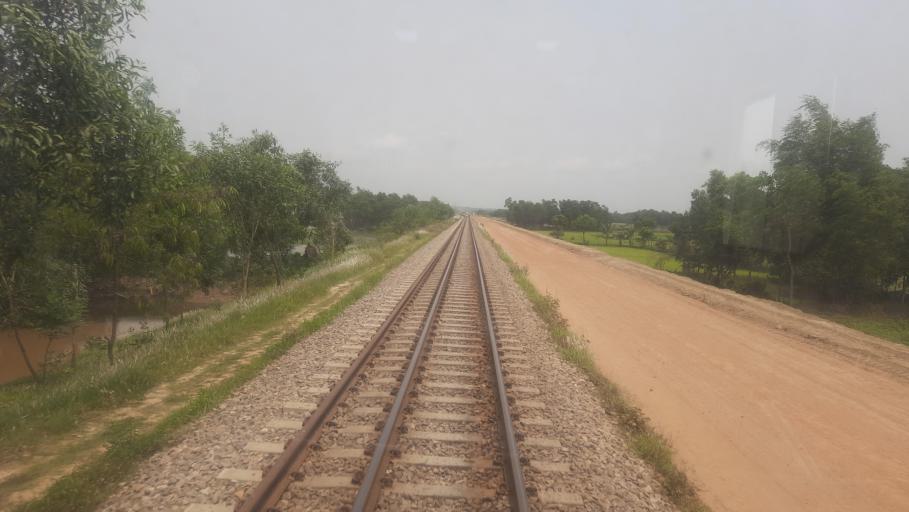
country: BD
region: Chittagong
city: Comilla
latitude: 23.6488
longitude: 91.1482
